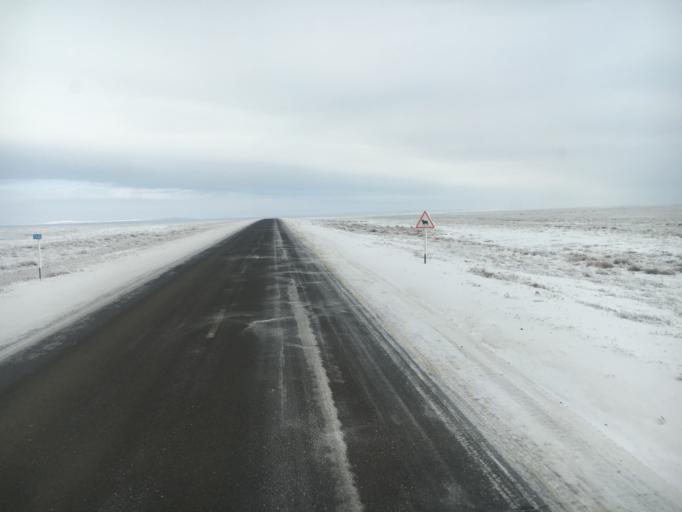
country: KZ
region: Aqtoebe
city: Yrghyz
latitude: 48.6936
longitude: 60.8348
